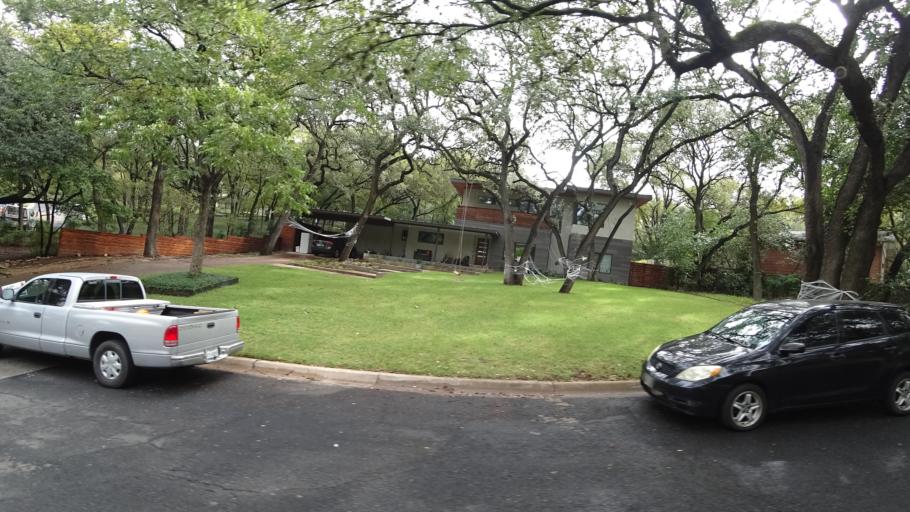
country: US
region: Texas
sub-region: Travis County
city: Rollingwood
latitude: 30.2569
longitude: -97.7779
